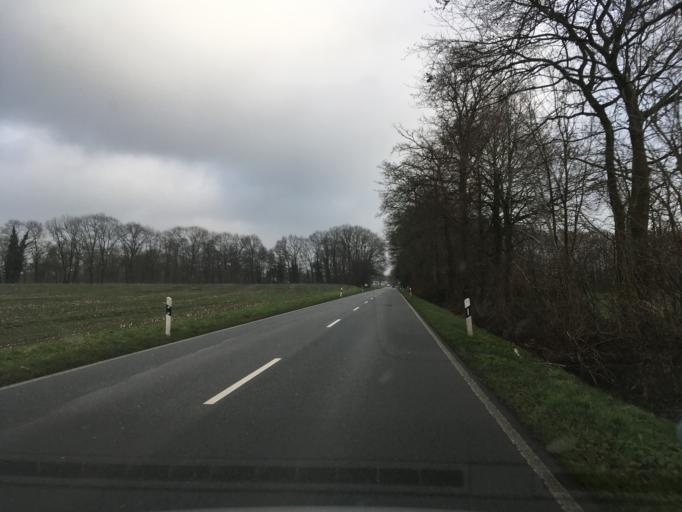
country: DE
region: North Rhine-Westphalia
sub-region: Regierungsbezirk Munster
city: Gronau
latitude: 52.2009
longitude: 7.0042
